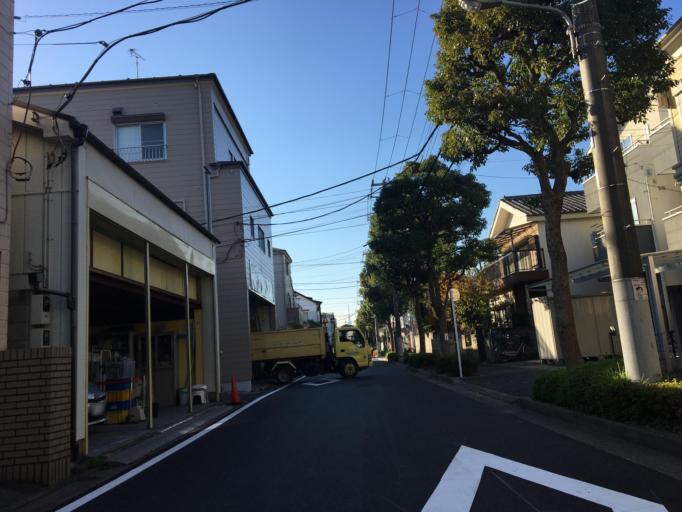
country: JP
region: Tokyo
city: Urayasu
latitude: 35.7134
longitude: 139.9004
